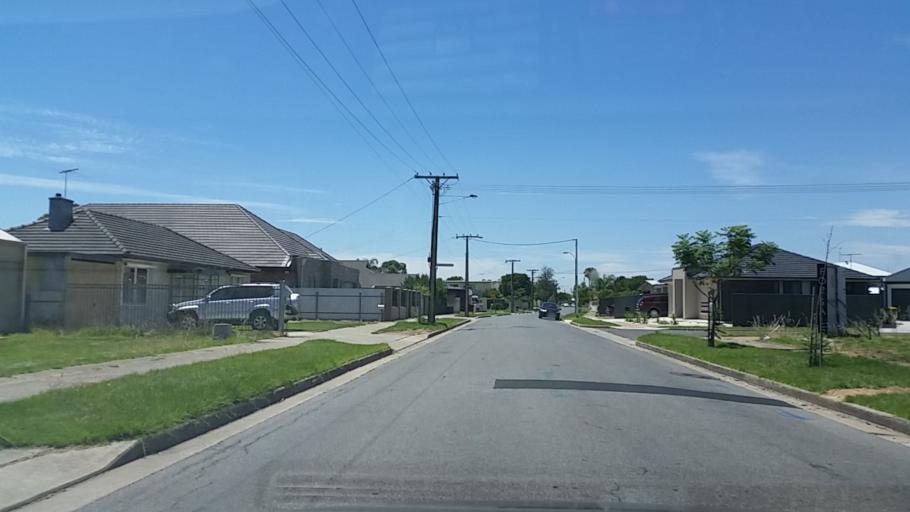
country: AU
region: South Australia
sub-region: Charles Sturt
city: Seaton
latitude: -34.8950
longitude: 138.5221
